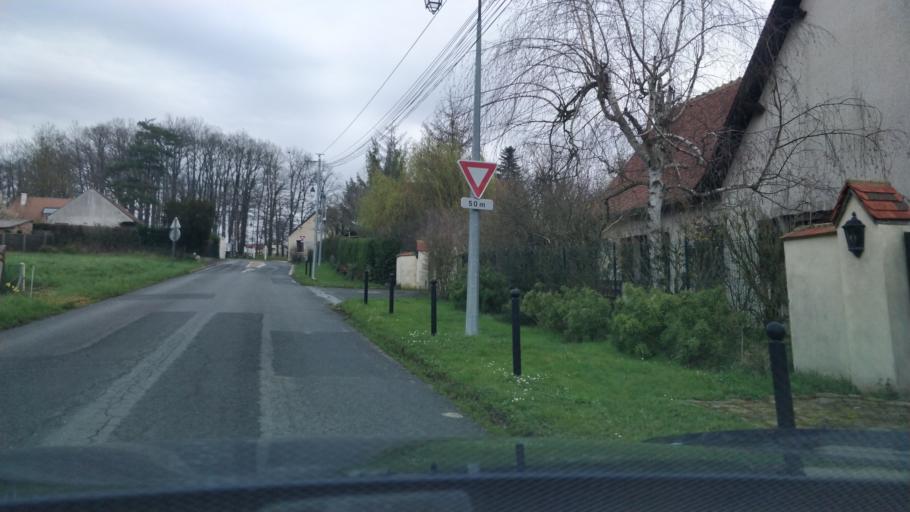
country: FR
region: Ile-de-France
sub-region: Departement de l'Essonne
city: Saint-Maurice-Montcouronne
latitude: 48.5907
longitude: 2.1100
